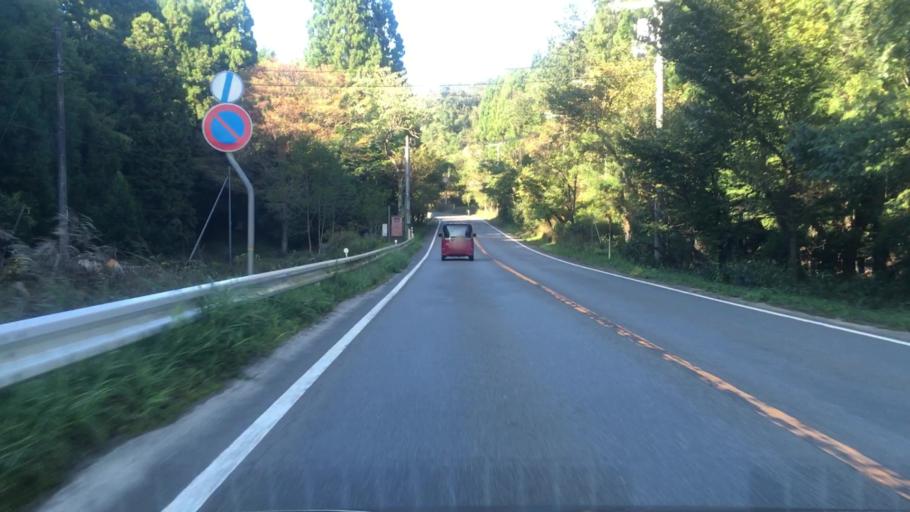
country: JP
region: Hyogo
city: Toyooka
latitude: 35.5644
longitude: 134.8524
